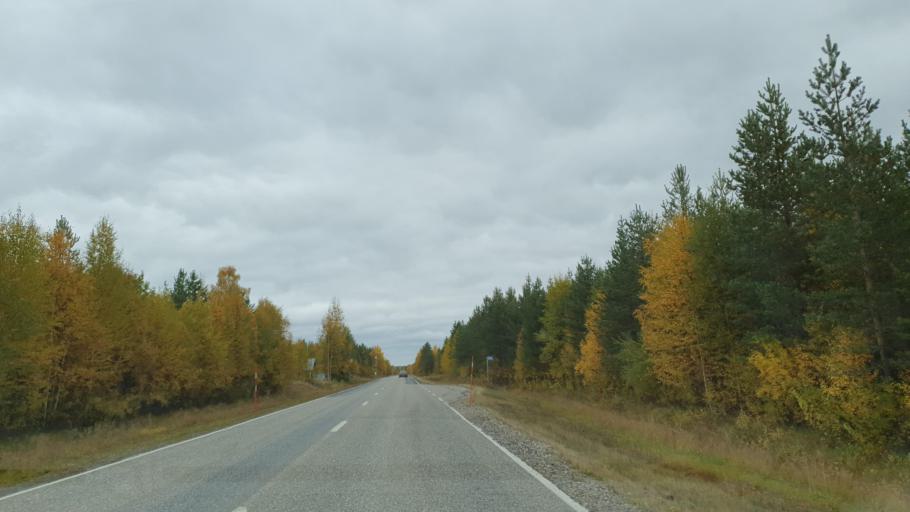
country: FI
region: Lapland
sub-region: Tunturi-Lappi
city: Kittilae
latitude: 67.1984
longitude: 24.9341
